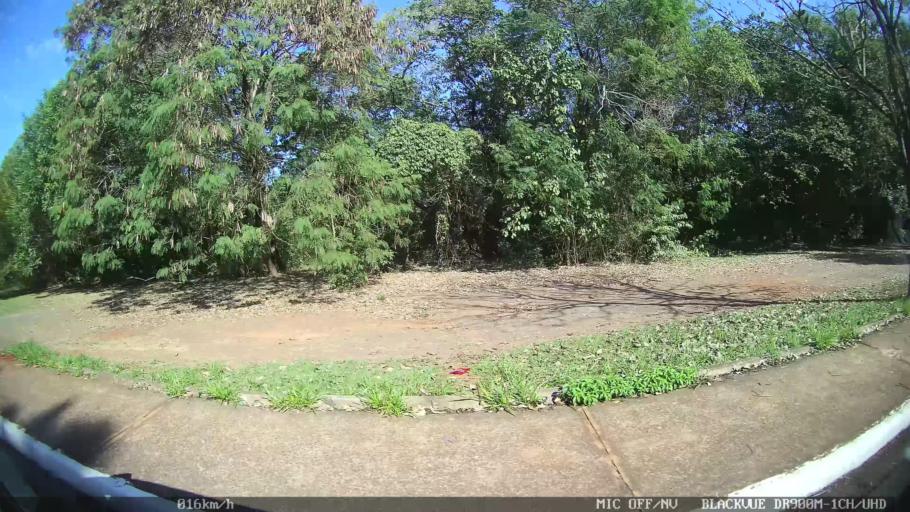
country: BR
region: Sao Paulo
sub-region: Americana
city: Americana
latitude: -22.7494
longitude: -47.3196
